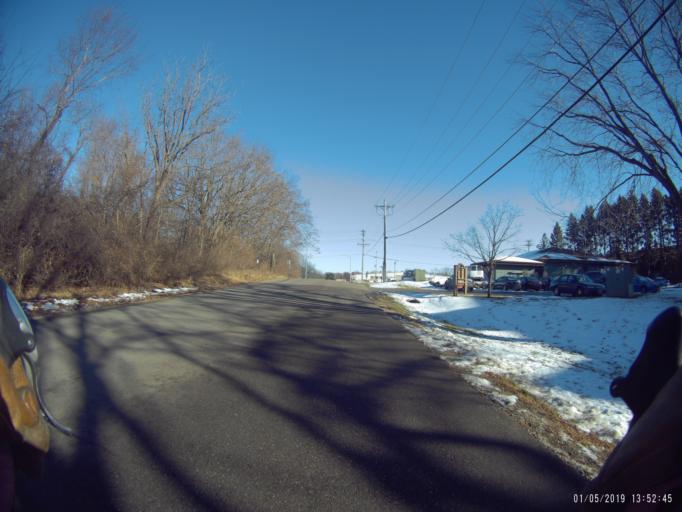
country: US
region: Wisconsin
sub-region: Dane County
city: Madison
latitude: 43.0446
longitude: -89.4051
